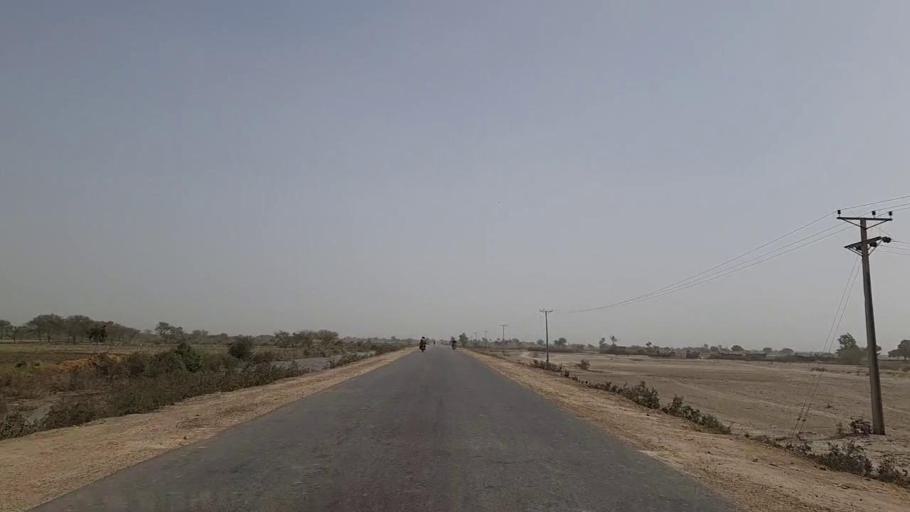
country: PK
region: Sindh
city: Talhar
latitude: 24.8688
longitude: 68.8426
